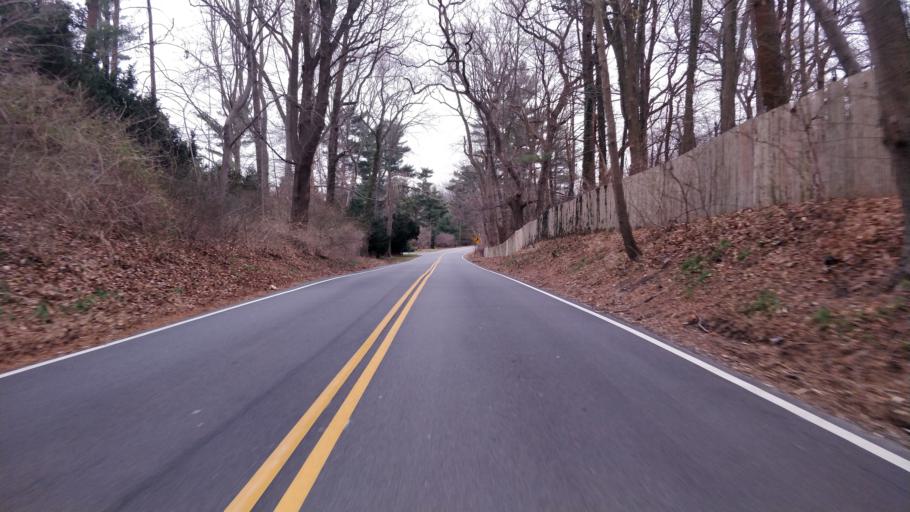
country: US
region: New York
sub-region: Nassau County
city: Old Westbury
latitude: 40.7785
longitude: -73.5915
